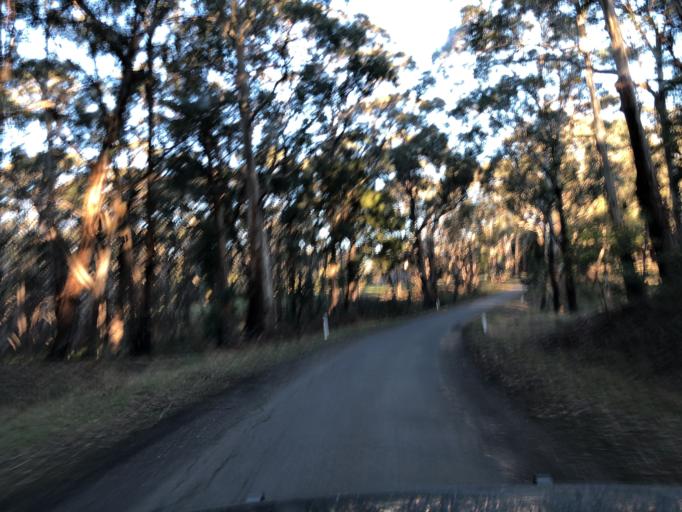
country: AU
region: Victoria
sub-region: Moorabool
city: Bacchus Marsh
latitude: -37.5137
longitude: 144.2149
